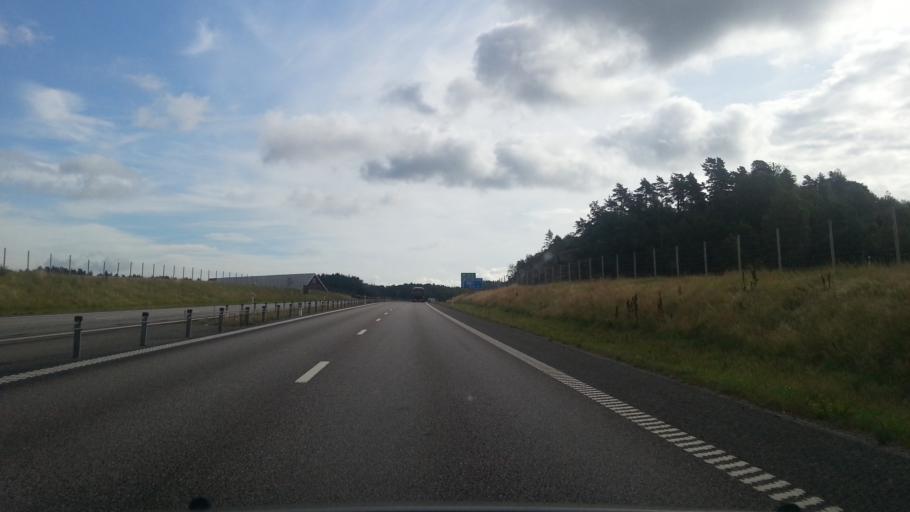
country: SE
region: Vaestra Goetaland
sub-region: Trollhattan
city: Sjuntorp
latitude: 58.2061
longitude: 12.1644
